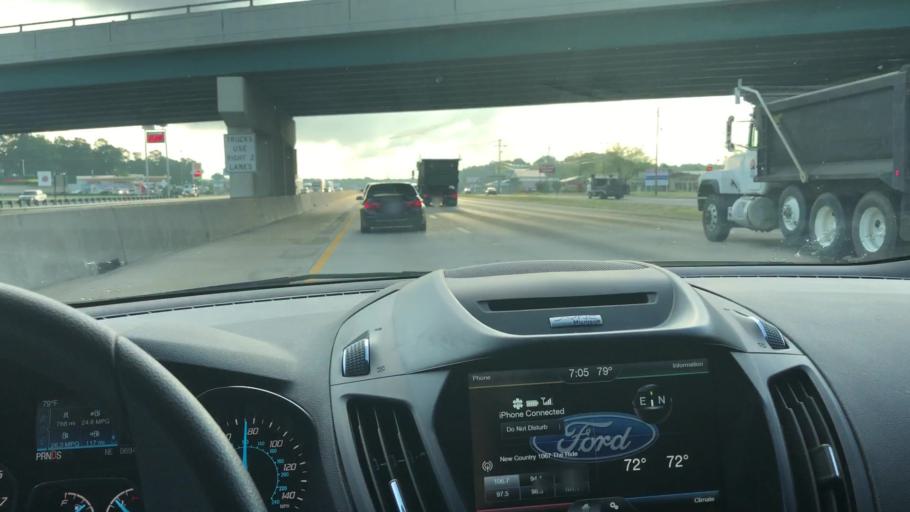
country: US
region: Arkansas
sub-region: Pulaski County
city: Alexander
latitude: 34.6405
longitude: -92.4449
